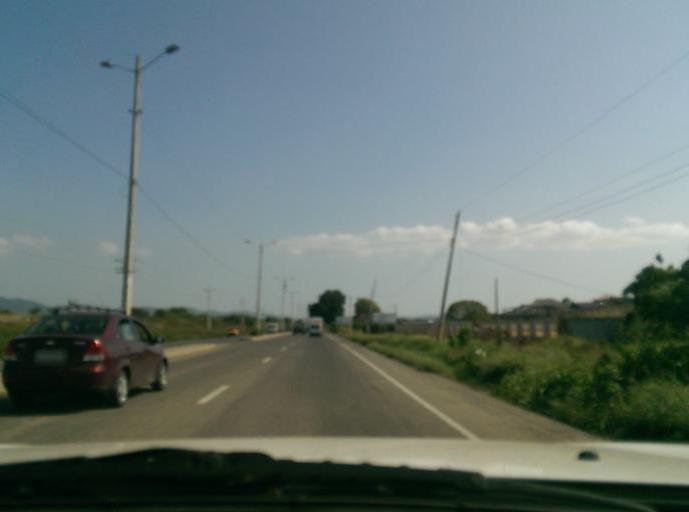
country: EC
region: Manabi
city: Manta
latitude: -0.9764
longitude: -80.6733
